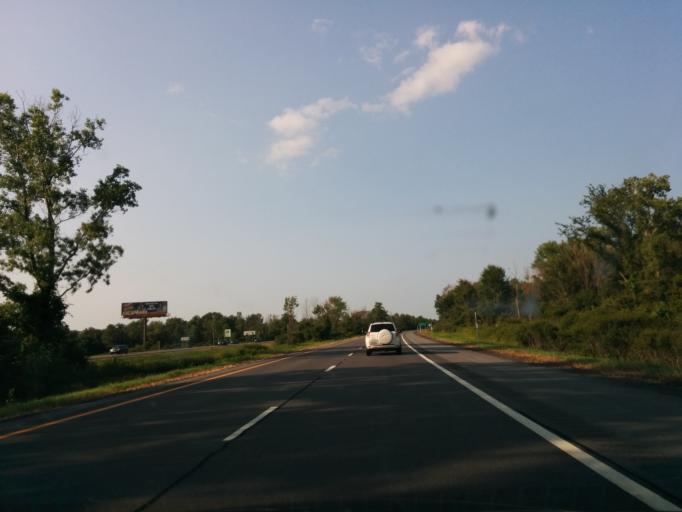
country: US
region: New York
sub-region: Oswego County
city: Pulaski
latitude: 43.6516
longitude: -76.0785
